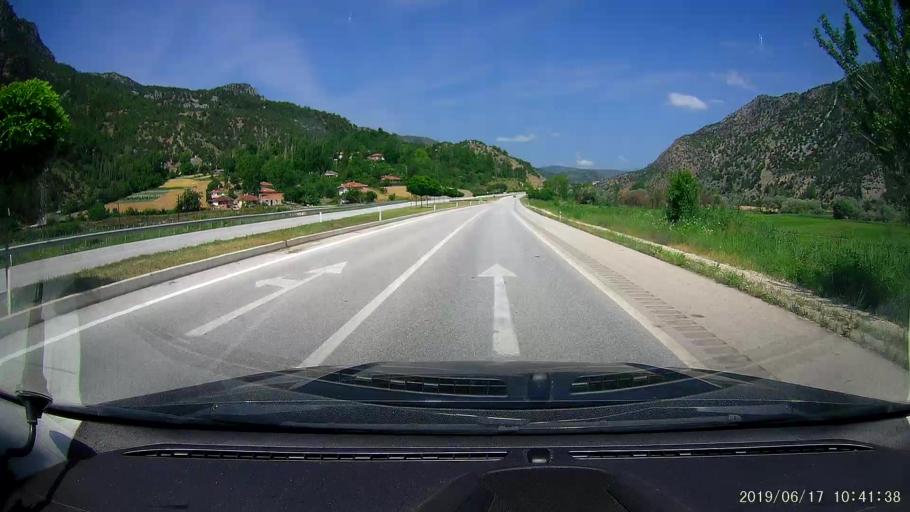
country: TR
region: Corum
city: Kargi
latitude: 41.0415
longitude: 34.5718
